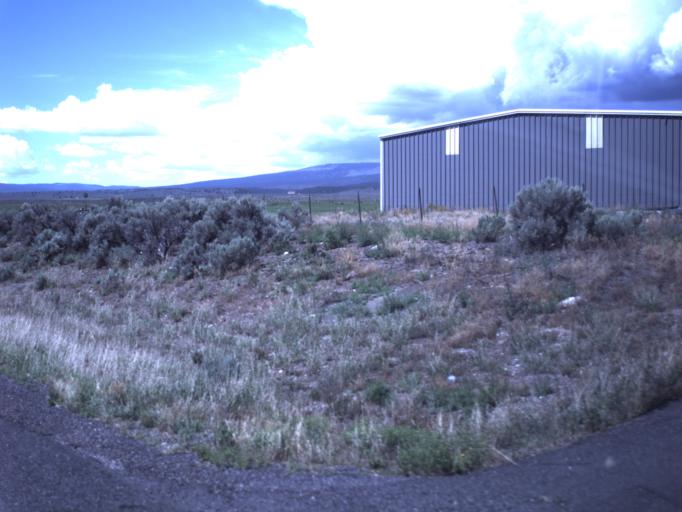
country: US
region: Utah
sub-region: Garfield County
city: Panguitch
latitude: 37.9016
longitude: -112.4316
